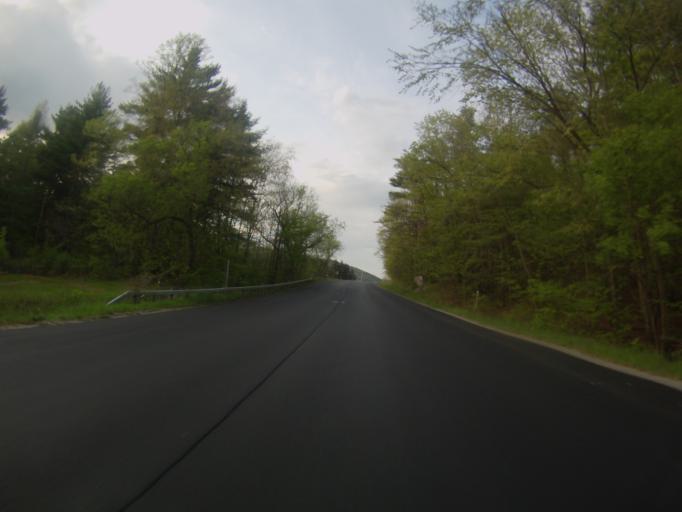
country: US
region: New York
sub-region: Essex County
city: Ticonderoga
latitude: 43.8182
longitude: -73.4748
